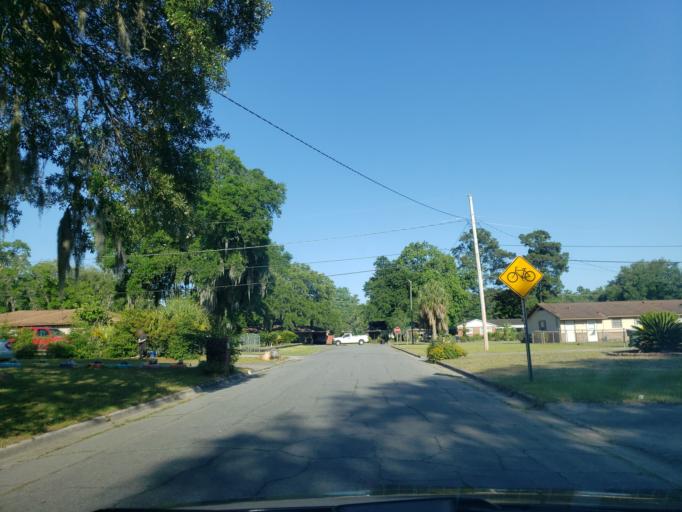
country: US
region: Georgia
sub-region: Chatham County
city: Montgomery
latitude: 31.9834
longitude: -81.1489
